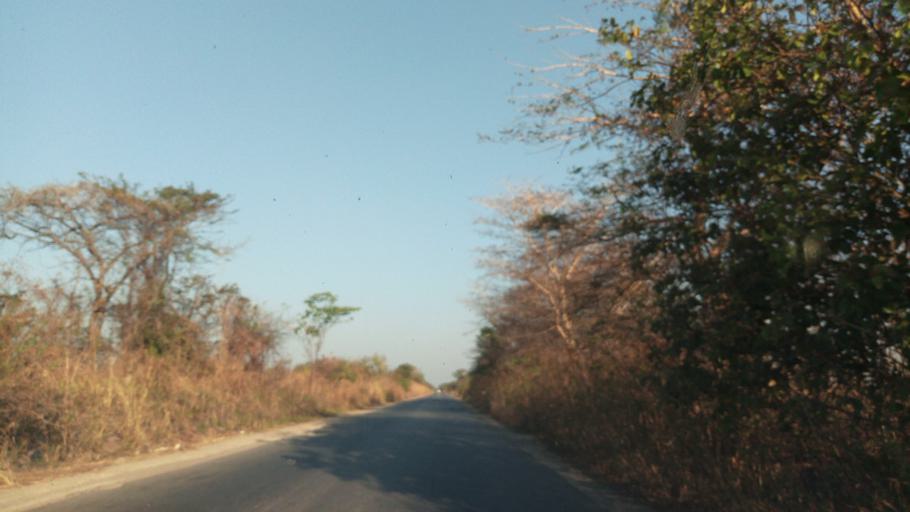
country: CD
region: Katanga
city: Likasi
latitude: -11.1108
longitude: 27.0225
